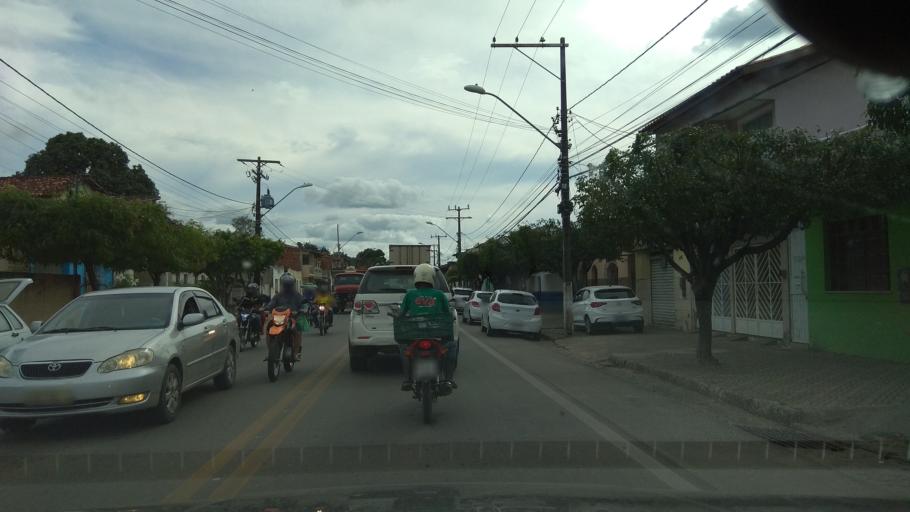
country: BR
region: Bahia
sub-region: Ipiau
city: Ipiau
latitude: -14.1348
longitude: -39.7467
